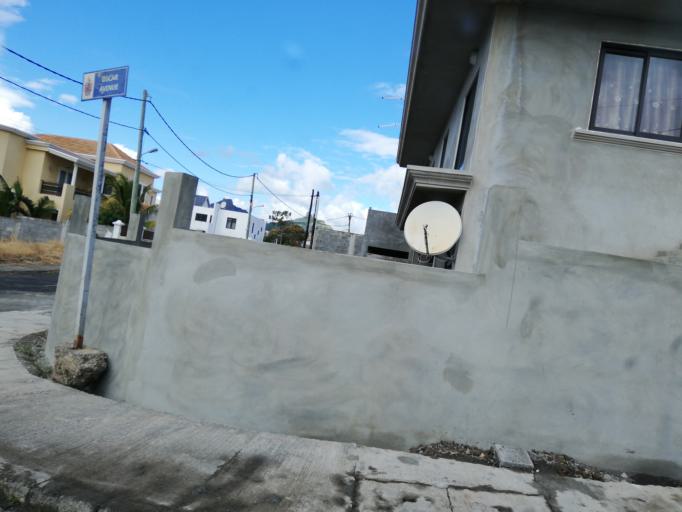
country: MU
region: Black River
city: Petite Riviere
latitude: -20.2029
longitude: 57.4623
